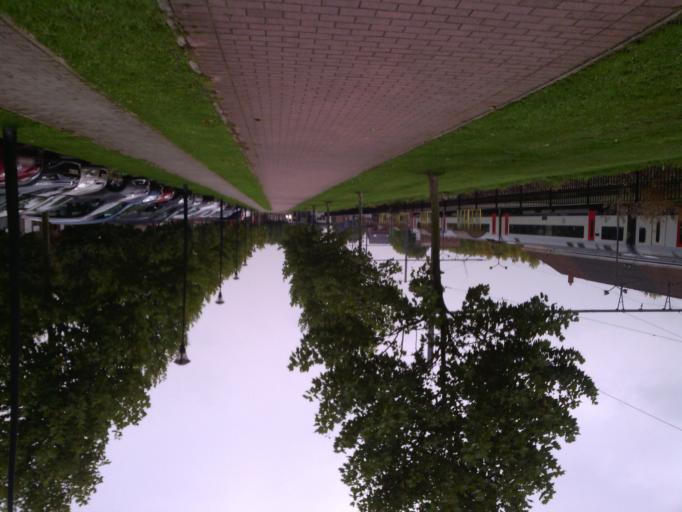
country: BE
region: Flanders
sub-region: Provincie West-Vlaanderen
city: Menen
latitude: 50.8008
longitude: 3.1148
